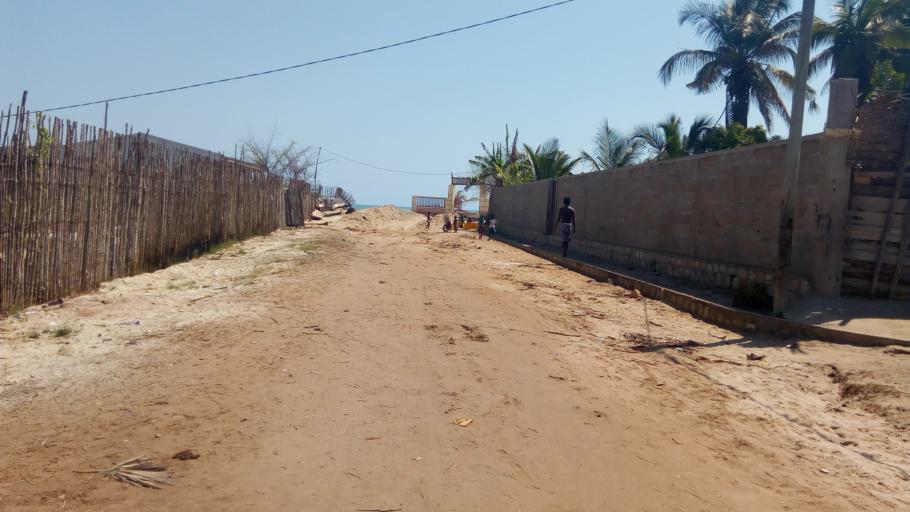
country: MG
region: Menabe
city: Morondava
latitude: -20.2922
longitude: 44.2724
